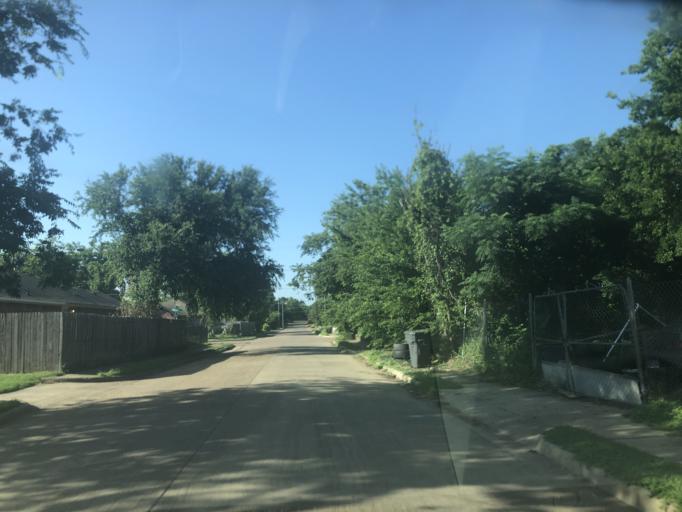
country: US
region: Texas
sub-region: Dallas County
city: Dallas
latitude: 32.7839
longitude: -96.8504
